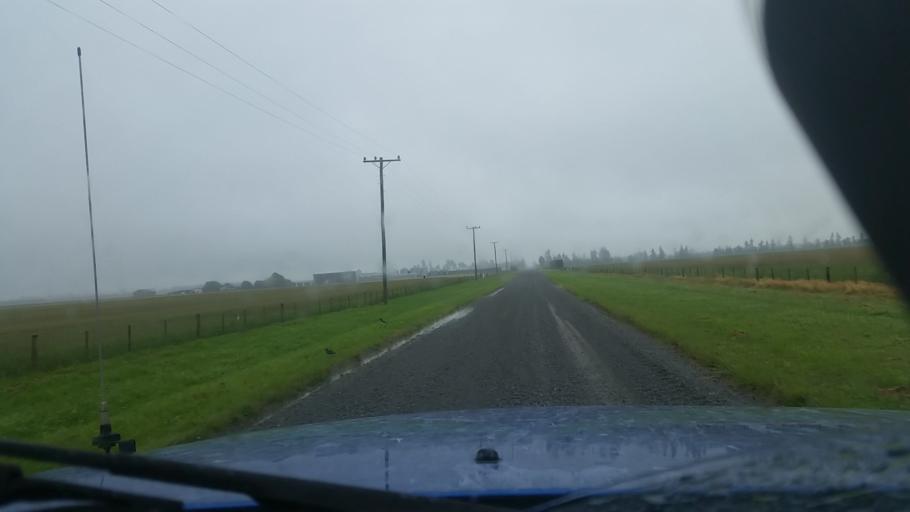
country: NZ
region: Canterbury
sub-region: Ashburton District
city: Rakaia
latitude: -43.6965
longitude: 171.8642
